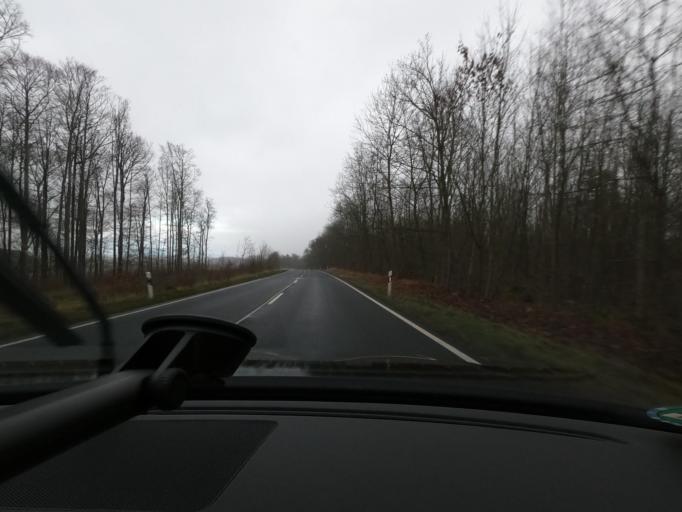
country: DE
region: Thuringia
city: Helmsdorf
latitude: 51.2768
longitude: 10.3642
